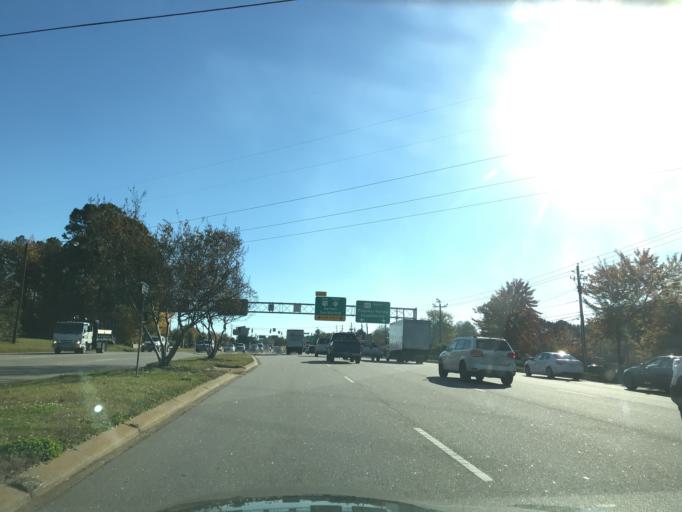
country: US
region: North Carolina
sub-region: Wake County
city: Raleigh
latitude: 35.7371
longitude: -78.6502
